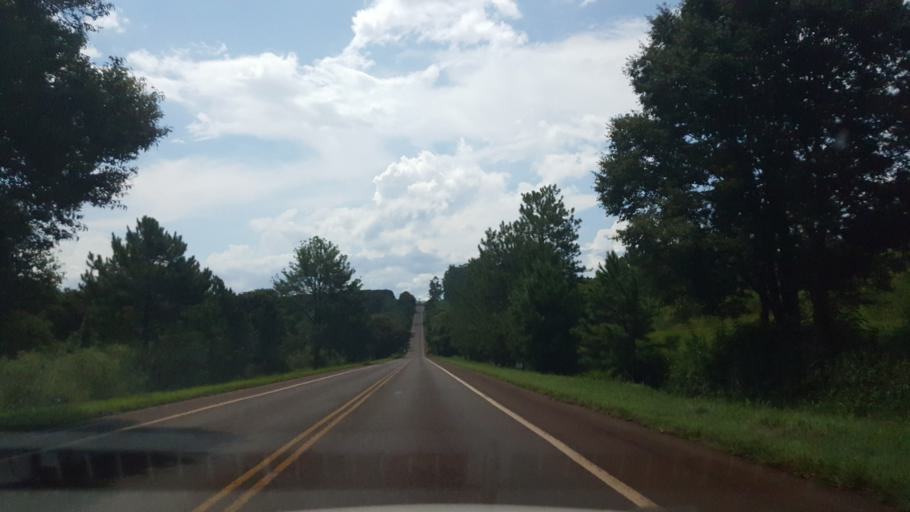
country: AR
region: Misiones
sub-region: Departamento de Eldorado
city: Eldorado
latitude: -26.3039
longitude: -54.6167
